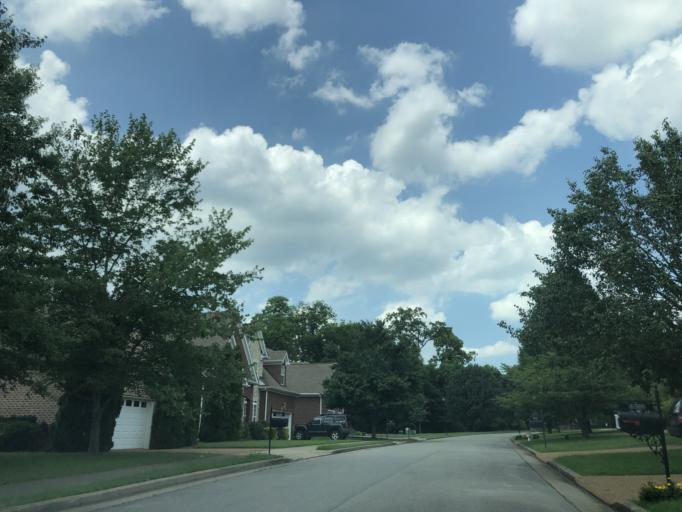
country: US
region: Tennessee
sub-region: Williamson County
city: Brentwood Estates
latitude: 36.0245
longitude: -86.7350
